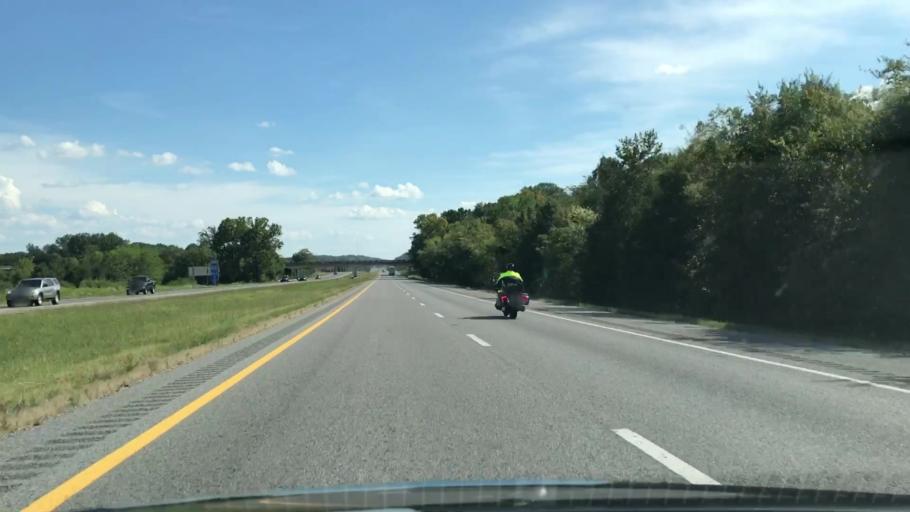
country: US
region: Alabama
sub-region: Limestone County
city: Ardmore
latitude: 35.0651
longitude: -86.8820
